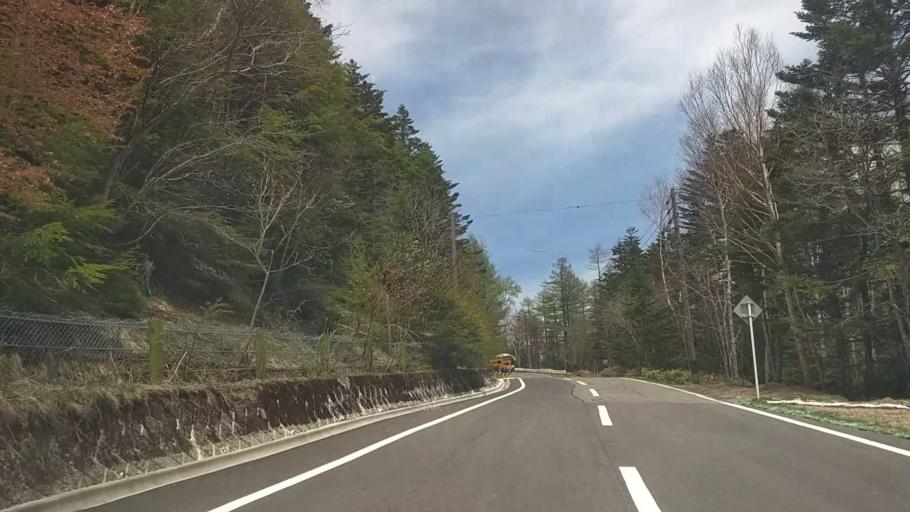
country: JP
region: Nagano
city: Saku
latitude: 36.0620
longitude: 138.3732
